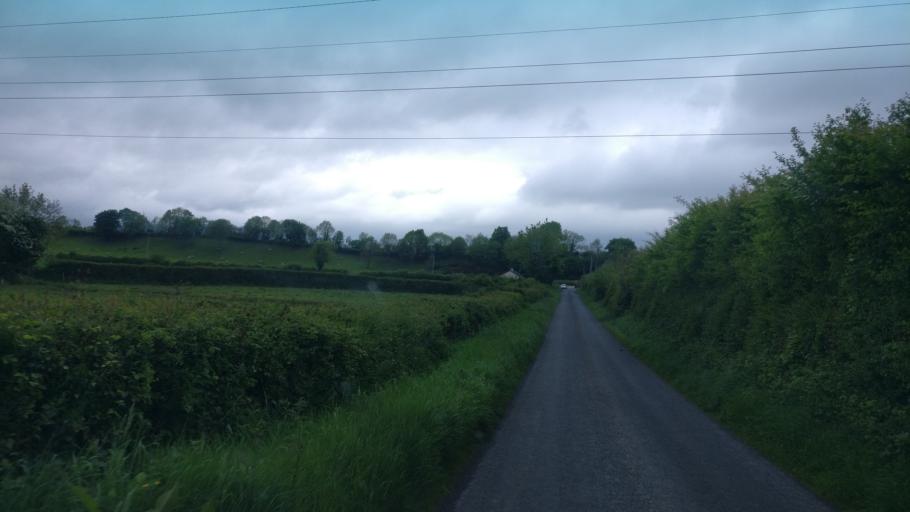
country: IE
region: Connaught
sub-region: County Galway
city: Portumna
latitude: 53.1393
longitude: -8.2906
